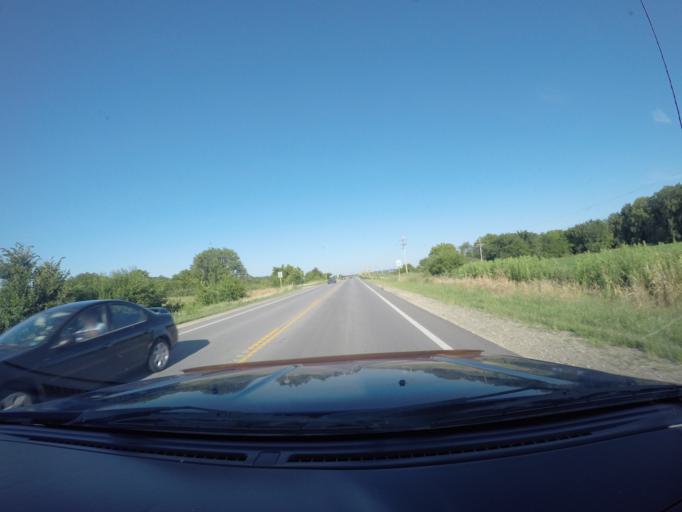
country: US
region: Kansas
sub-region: Douglas County
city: Lawrence
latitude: 39.0670
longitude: -95.3370
